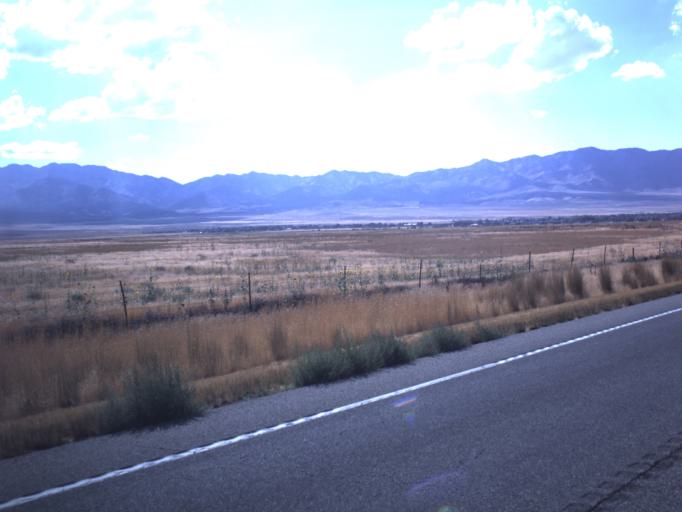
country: US
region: Utah
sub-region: Tooele County
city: Grantsville
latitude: 40.5778
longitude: -112.3920
